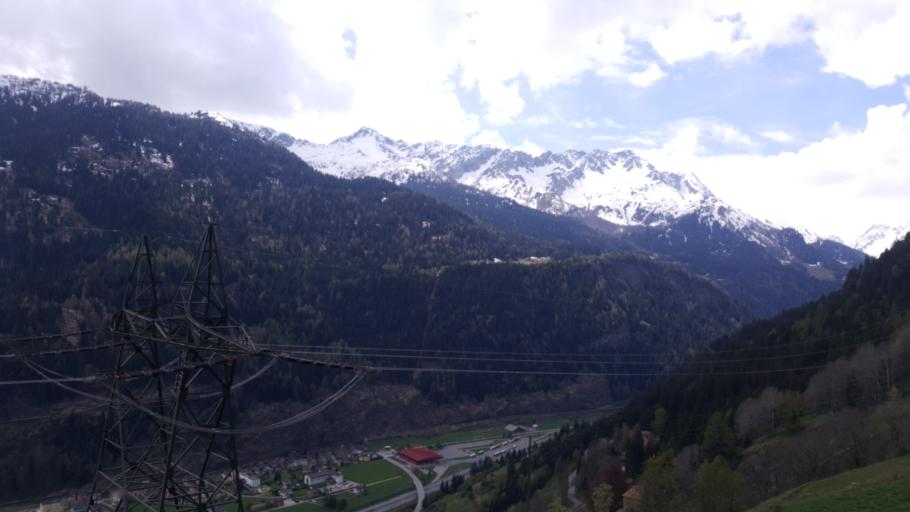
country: CH
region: Ticino
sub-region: Leventina District
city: Airolo
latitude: 46.5218
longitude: 8.6797
